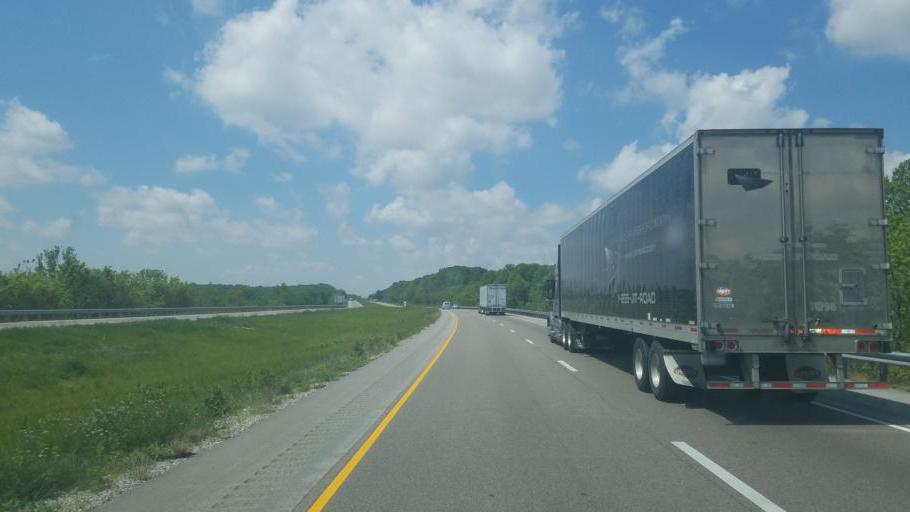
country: US
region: Illinois
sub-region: Cumberland County
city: Greenup
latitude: 39.2516
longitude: -88.1795
